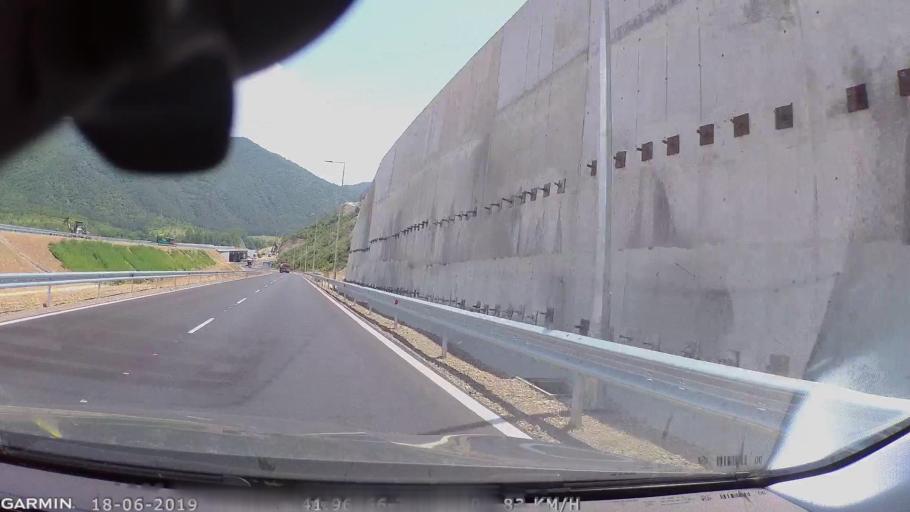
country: BG
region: Blagoevgrad
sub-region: Obshtina Blagoevgrad
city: Blagoevgrad
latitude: 41.9641
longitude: 23.0956
